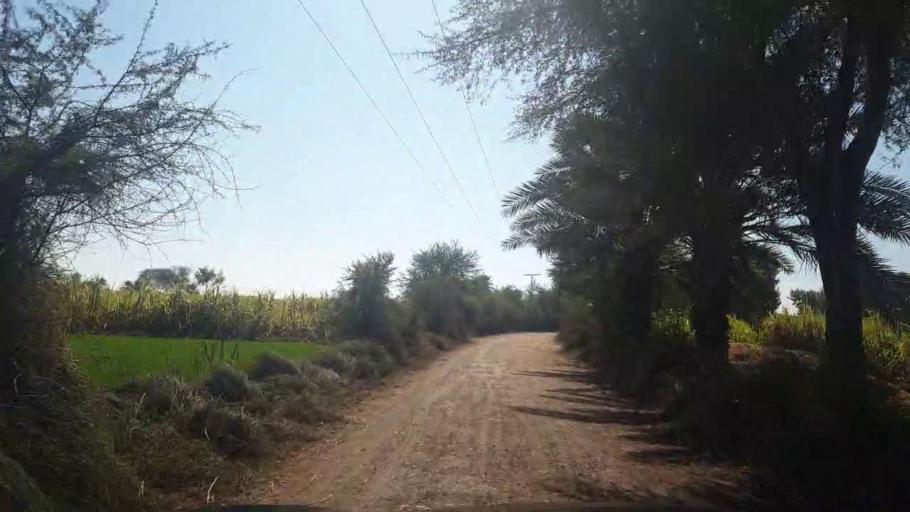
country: PK
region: Sindh
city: Adilpur
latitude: 27.9426
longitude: 69.3373
